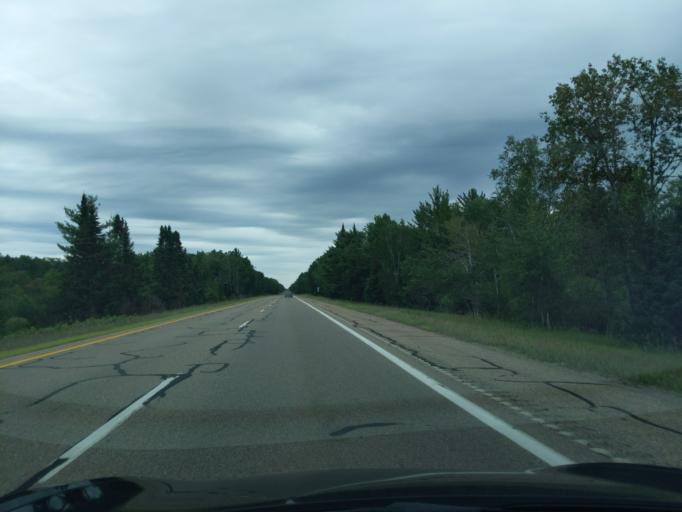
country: US
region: Michigan
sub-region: Roscommon County
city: Houghton Lake
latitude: 44.2191
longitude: -84.7969
